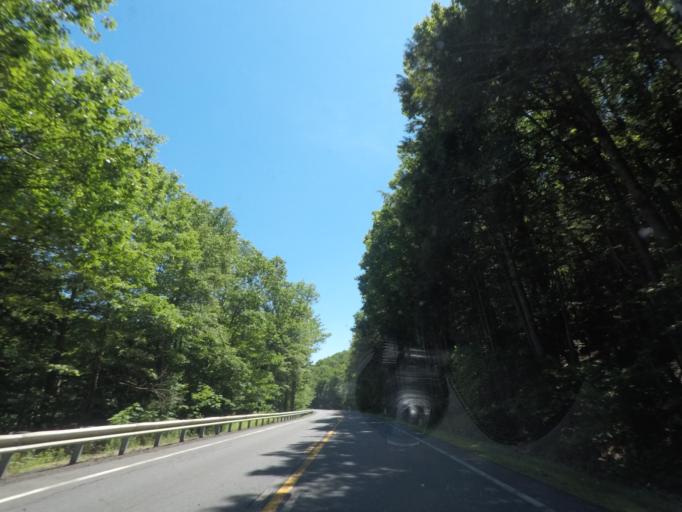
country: US
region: Massachusetts
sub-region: Hampshire County
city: Westhampton
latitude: 42.2416
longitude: -72.9141
